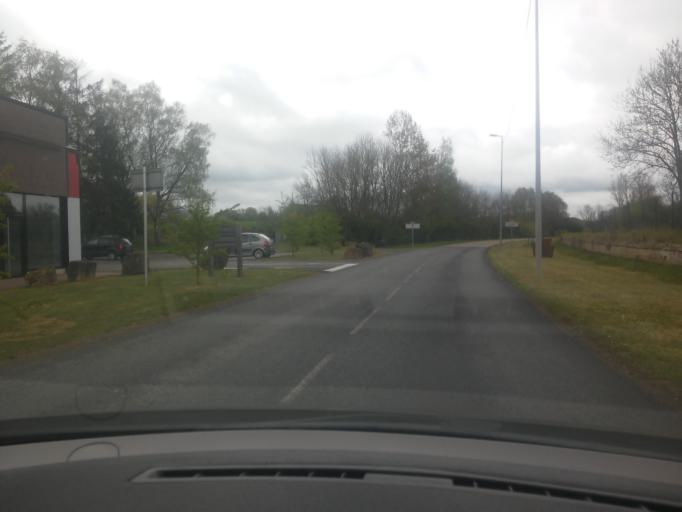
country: FR
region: Lorraine
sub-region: Departement de la Moselle
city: Courcelles-Chaussy
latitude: 49.1066
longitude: 6.3927
